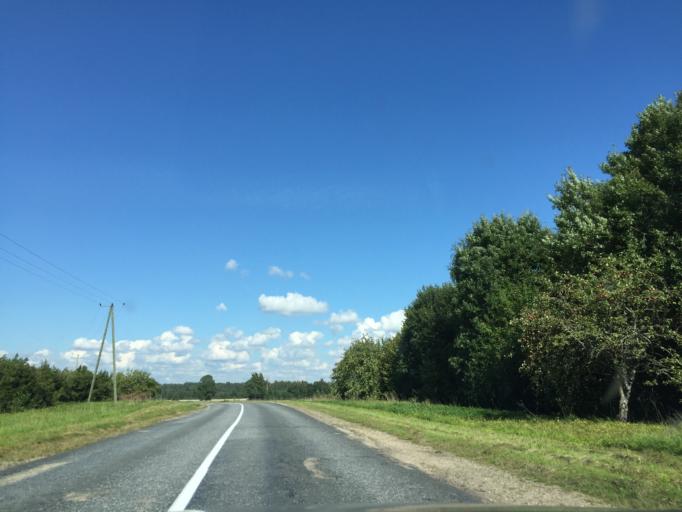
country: LV
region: Limbazu Rajons
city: Limbazi
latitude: 57.4305
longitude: 24.7133
